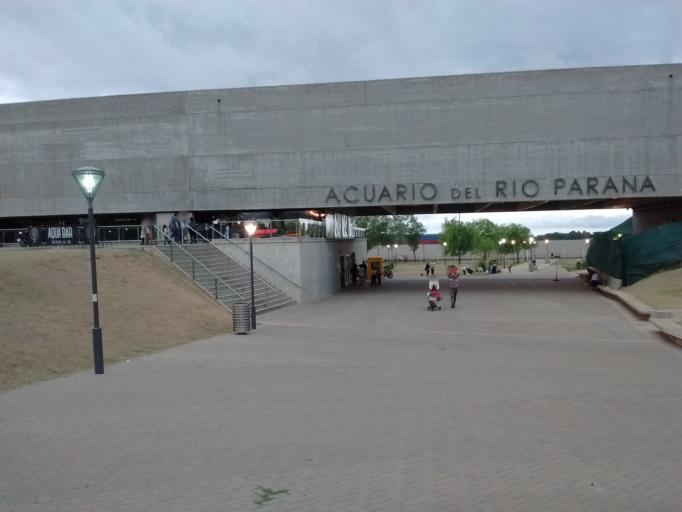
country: AR
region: Santa Fe
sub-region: Departamento de Rosario
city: Rosario
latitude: -32.9116
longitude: -60.6755
